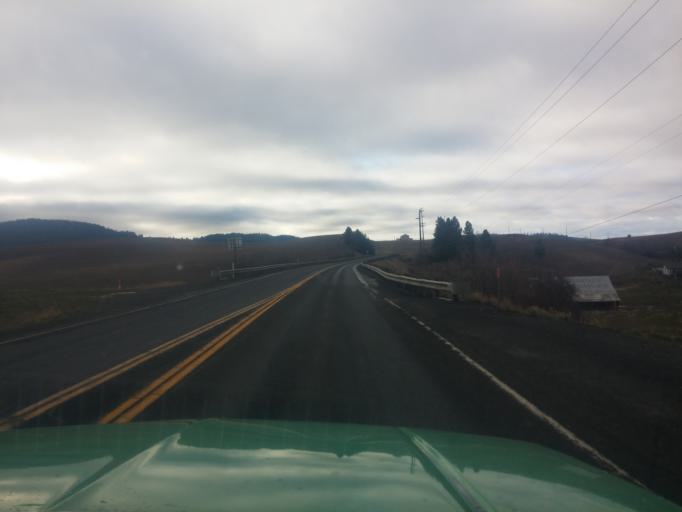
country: US
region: Idaho
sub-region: Latah County
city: Moscow
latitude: 46.8544
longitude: -117.0212
